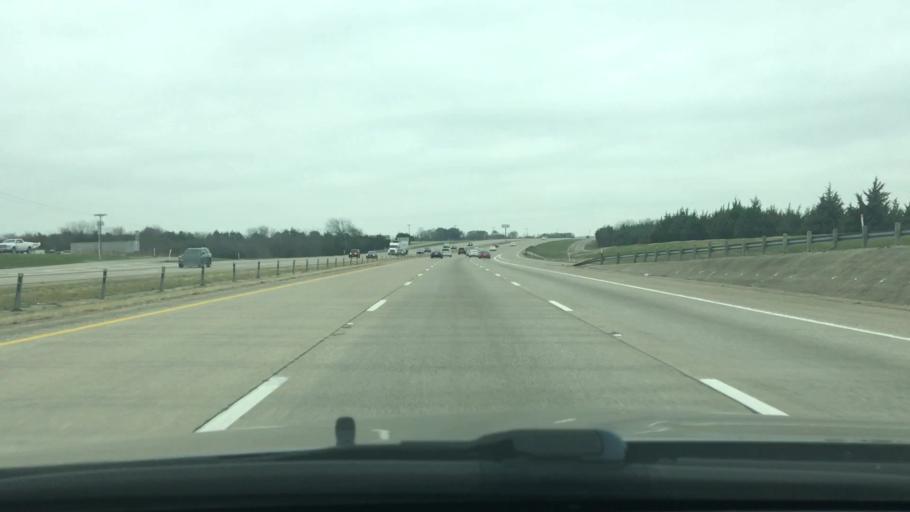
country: US
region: Texas
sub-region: Ellis County
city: Palmer
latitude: 32.4314
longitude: -96.6595
